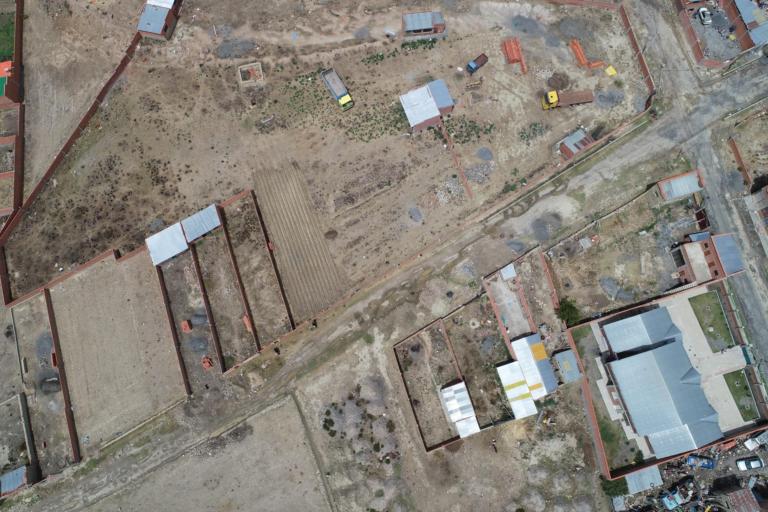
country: BO
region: La Paz
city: Achacachi
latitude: -16.0539
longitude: -68.6816
